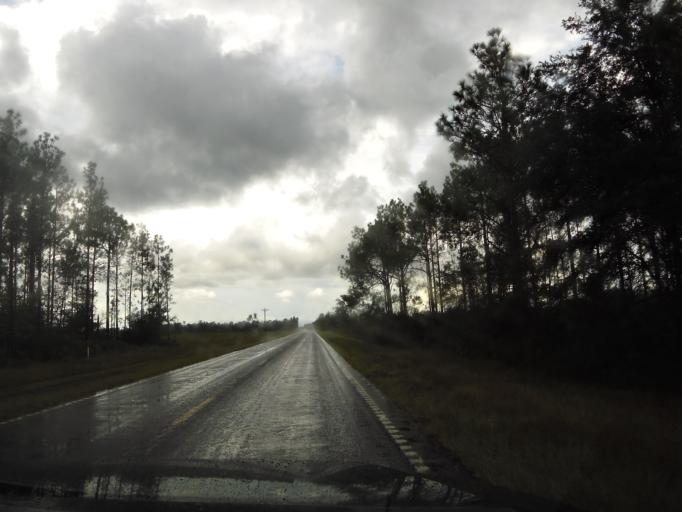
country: US
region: Florida
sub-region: Nassau County
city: Hilliard
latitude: 30.5453
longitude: -82.0406
